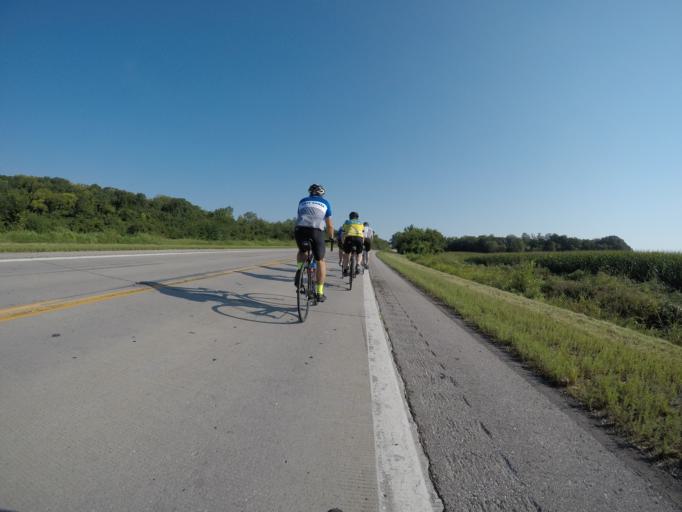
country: US
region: Missouri
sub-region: Platte County
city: Weston
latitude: 39.3849
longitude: -94.8651
